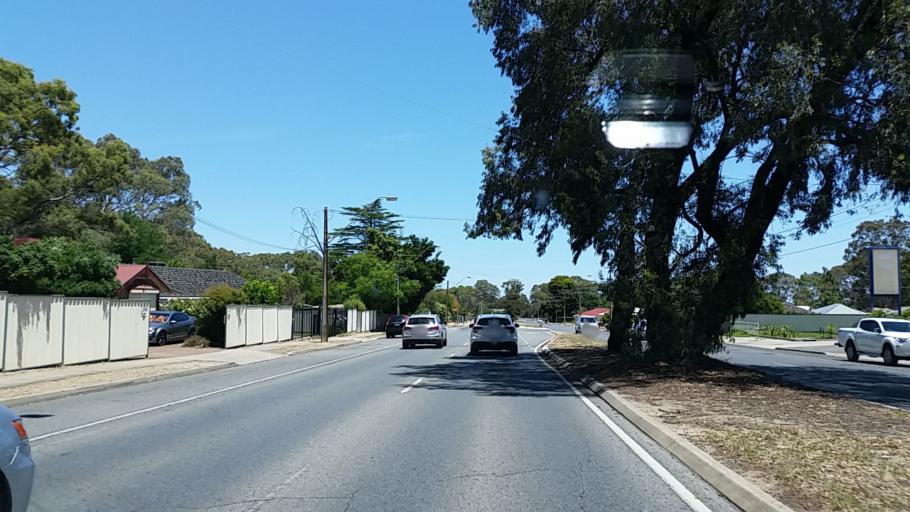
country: AU
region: South Australia
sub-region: Tea Tree Gully
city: Hope Valley
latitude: -34.8236
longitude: 138.7102
